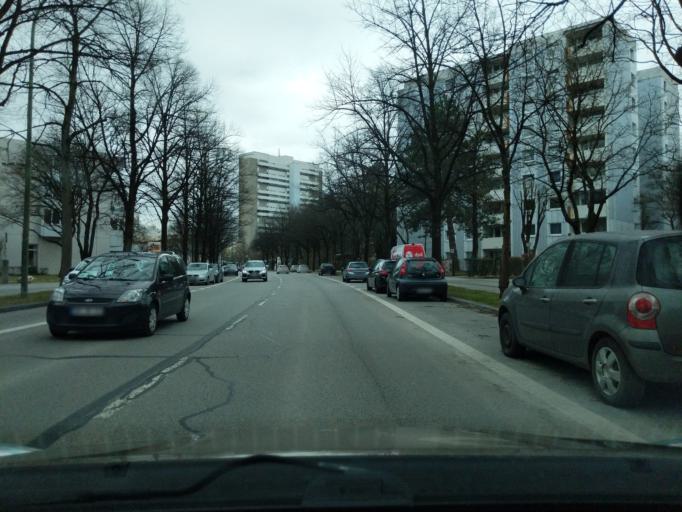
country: DE
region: Bavaria
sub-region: Upper Bavaria
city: Bogenhausen
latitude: 48.1603
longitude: 11.6436
